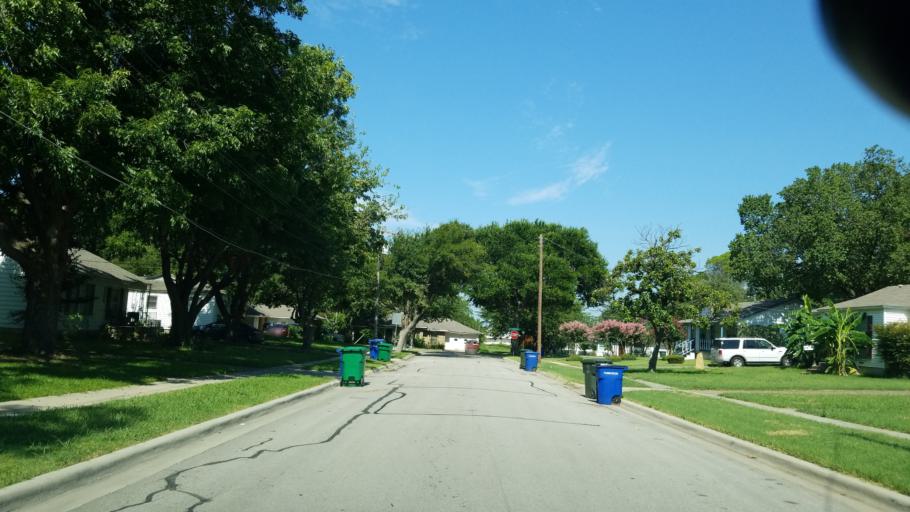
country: US
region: Texas
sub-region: Dallas County
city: Carrollton
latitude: 32.9660
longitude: -96.9100
